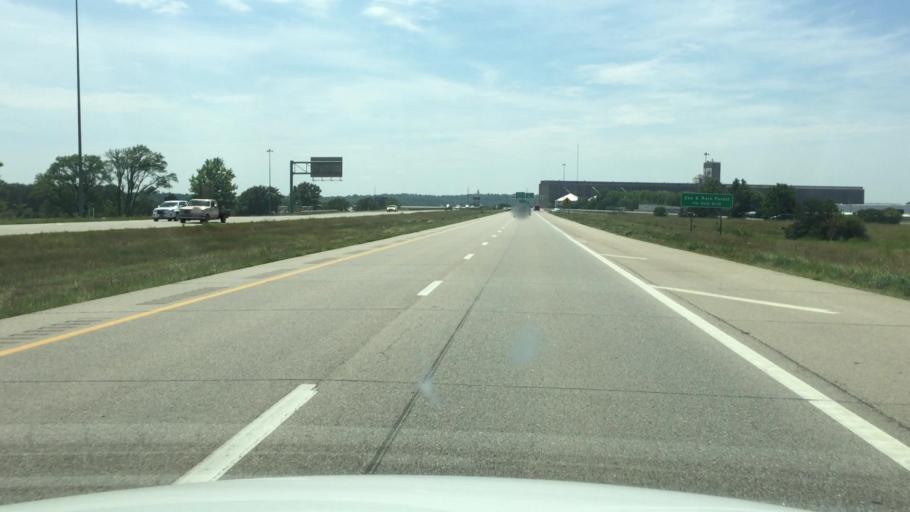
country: US
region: Kansas
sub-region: Shawnee County
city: Topeka
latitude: 39.0931
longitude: -95.7248
